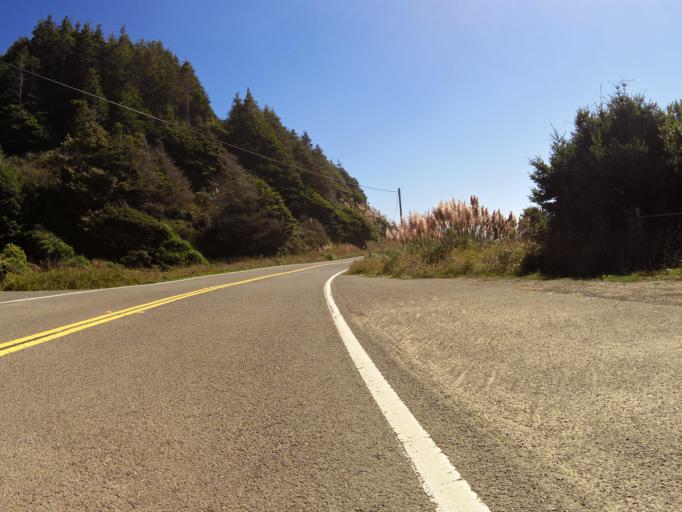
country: US
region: California
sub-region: Mendocino County
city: Fort Bragg
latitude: 39.6986
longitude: -123.8006
